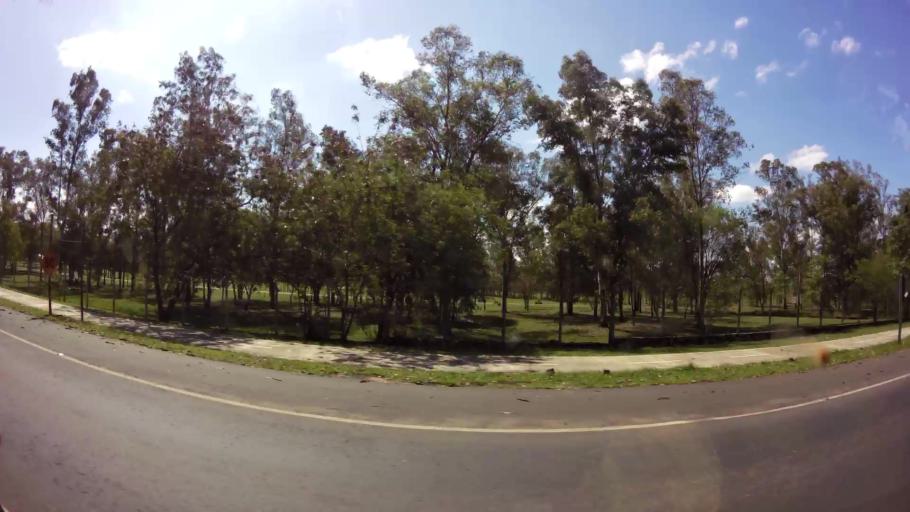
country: PY
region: Central
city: Fernando de la Mora
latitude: -25.2729
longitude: -57.5404
